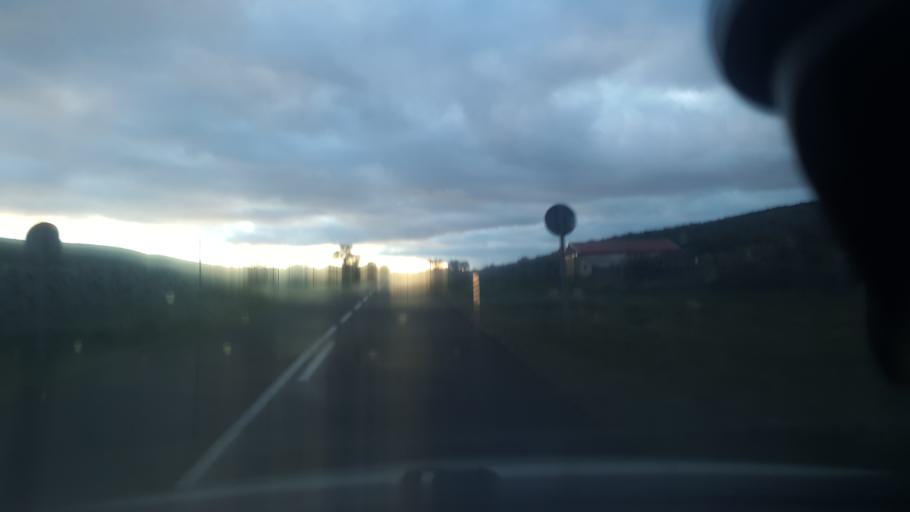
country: ES
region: Castille and Leon
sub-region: Provincia de Segovia
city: Vegas de Matute
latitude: 40.7166
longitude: -4.3065
